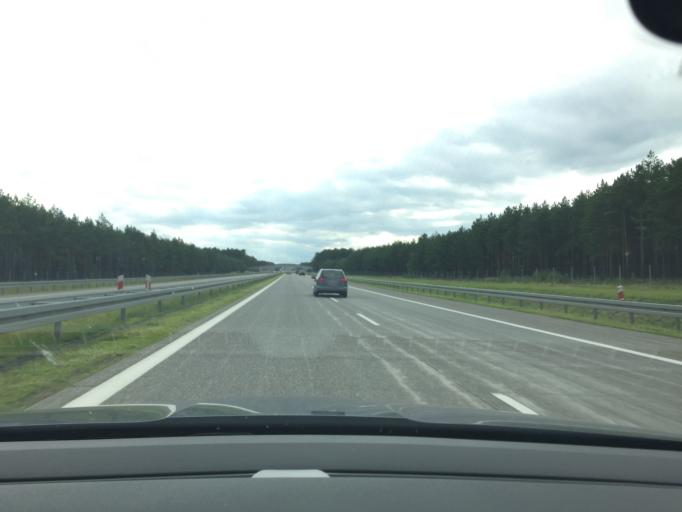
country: PL
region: Greater Poland Voivodeship
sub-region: Powiat nowotomyski
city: Nowy Tomysl
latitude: 52.3524
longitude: 16.0628
